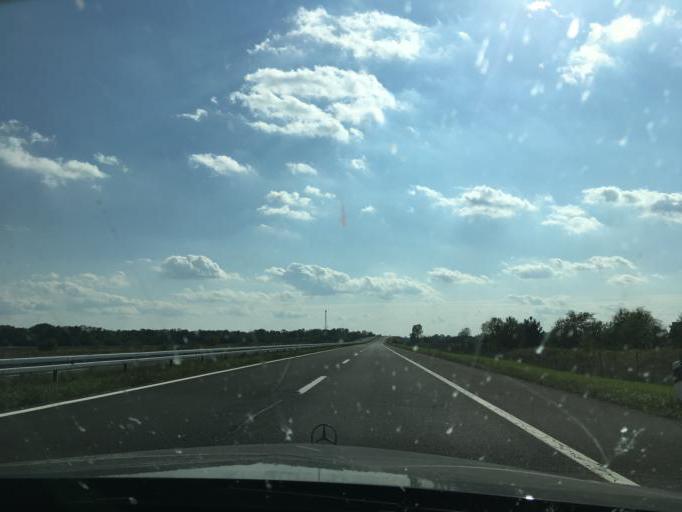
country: HR
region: Medimurska
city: Palovec
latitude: 46.3843
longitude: 16.5566
